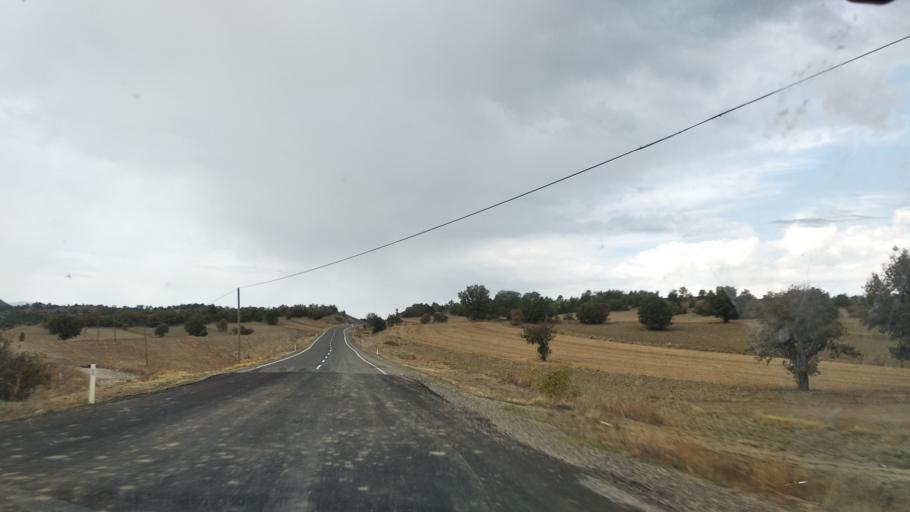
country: TR
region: Bolu
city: Seben
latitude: 40.3329
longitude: 31.4492
